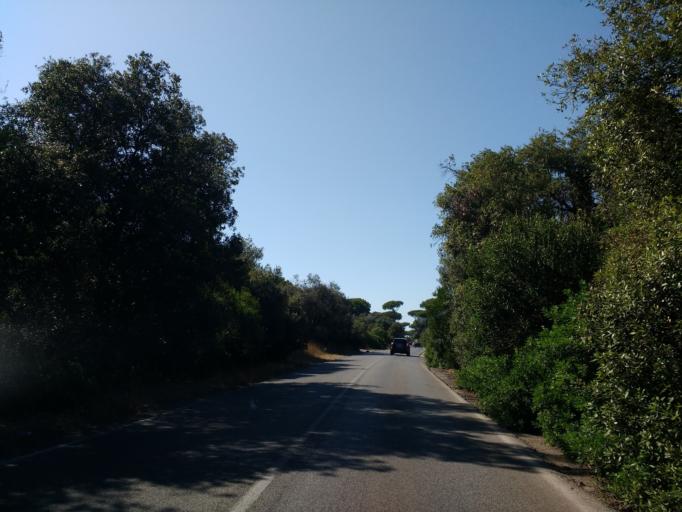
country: IT
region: Latium
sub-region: Citta metropolitana di Roma Capitale
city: Acilia-Castel Fusano-Ostia Antica
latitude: 41.7178
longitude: 12.3513
